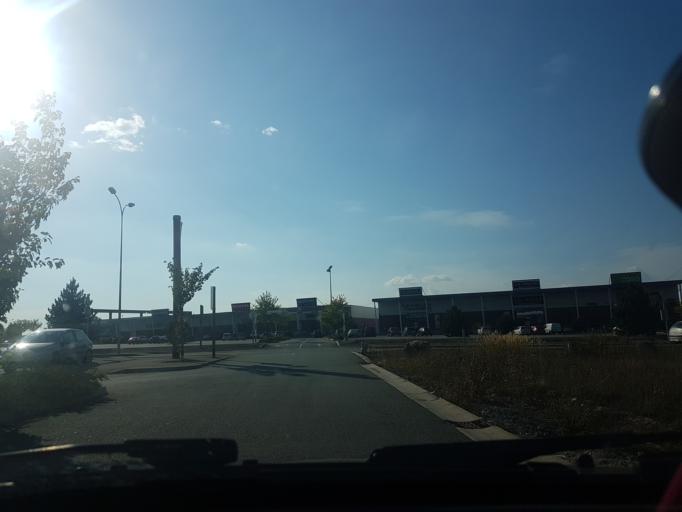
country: FR
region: Franche-Comte
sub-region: Territoire de Belfort
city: Chevremont
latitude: 47.6423
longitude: 6.9207
